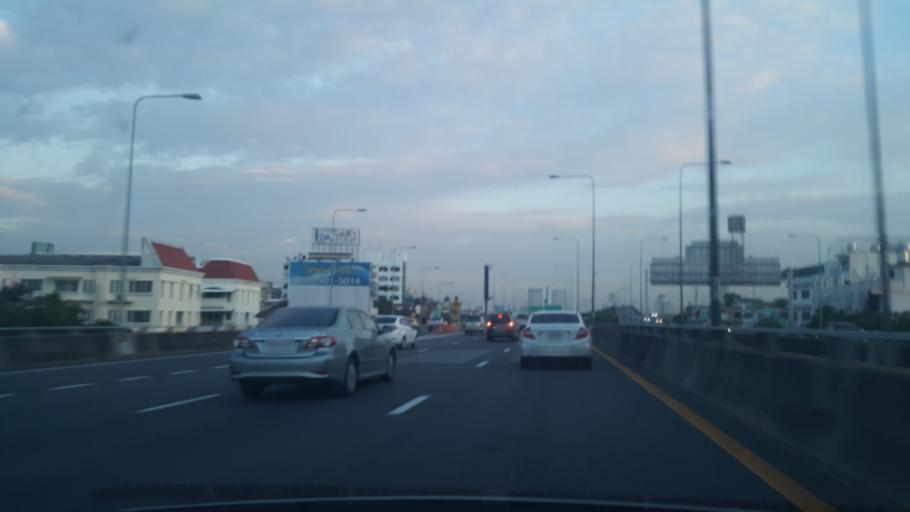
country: TH
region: Bangkok
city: Sathon
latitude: 13.6965
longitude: 100.5237
